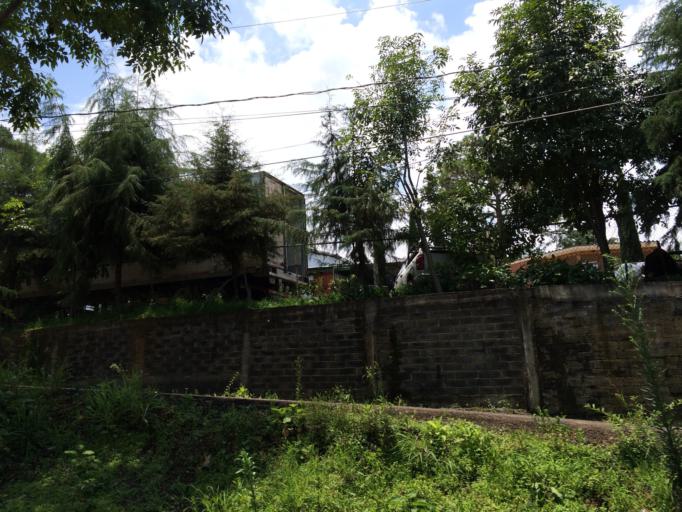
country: MX
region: Michoacan
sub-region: Periban
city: San Francisco Periban
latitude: 19.5419
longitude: -102.4075
